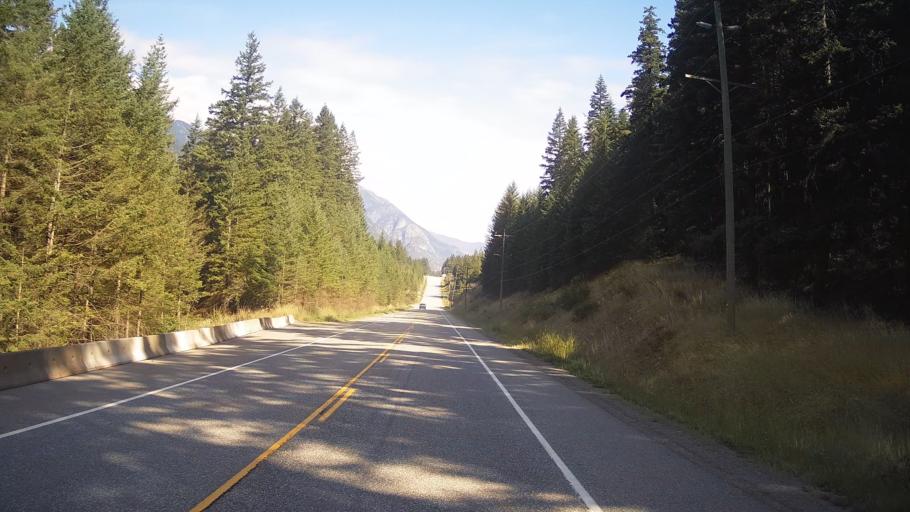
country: CA
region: British Columbia
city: Hope
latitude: 50.0277
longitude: -121.5283
